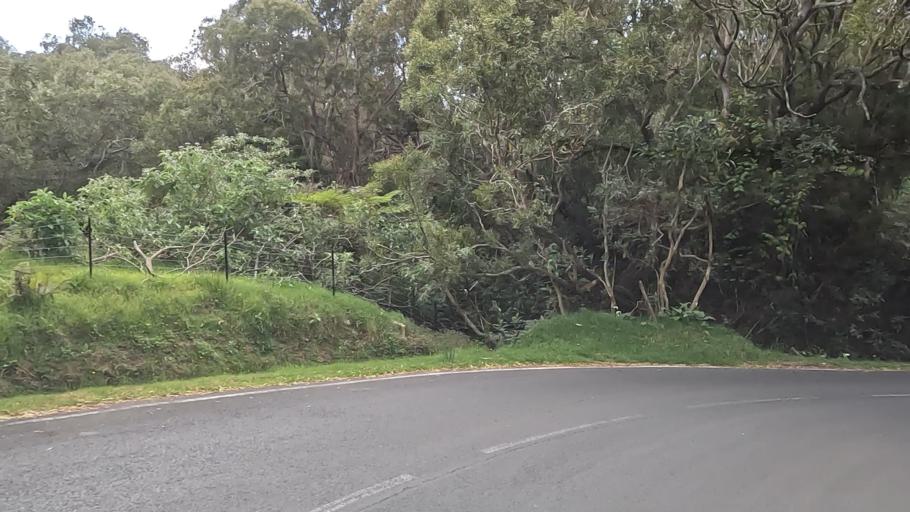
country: RE
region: Reunion
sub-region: Reunion
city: Le Tampon
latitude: -21.2410
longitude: 55.5863
